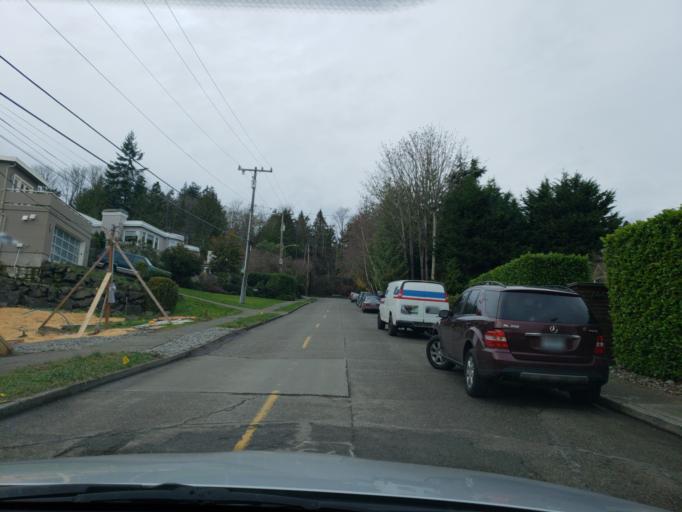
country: US
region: Washington
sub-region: King County
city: Seattle
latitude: 47.6661
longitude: -122.4076
